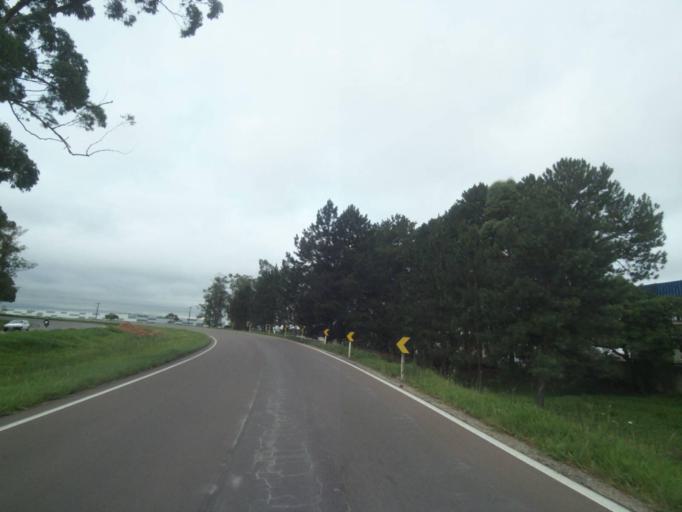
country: BR
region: Parana
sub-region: Sao Jose Dos Pinhais
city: Sao Jose dos Pinhais
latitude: -25.5392
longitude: -49.3106
